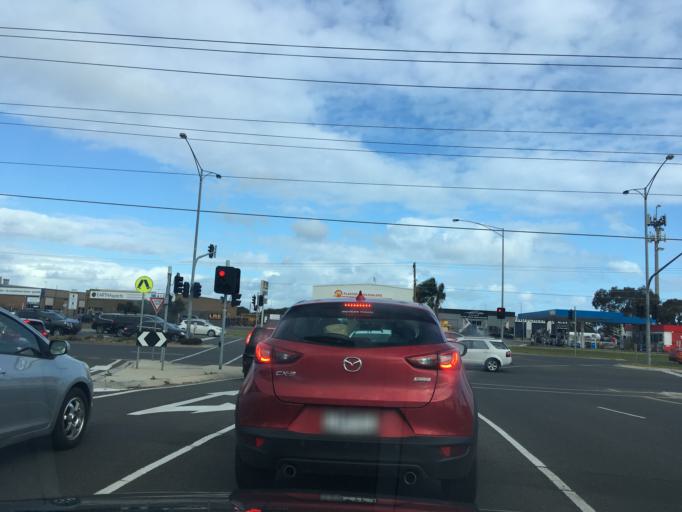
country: AU
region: Victoria
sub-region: Wyndham
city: Hoppers Crossing
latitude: -37.8764
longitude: 144.7134
